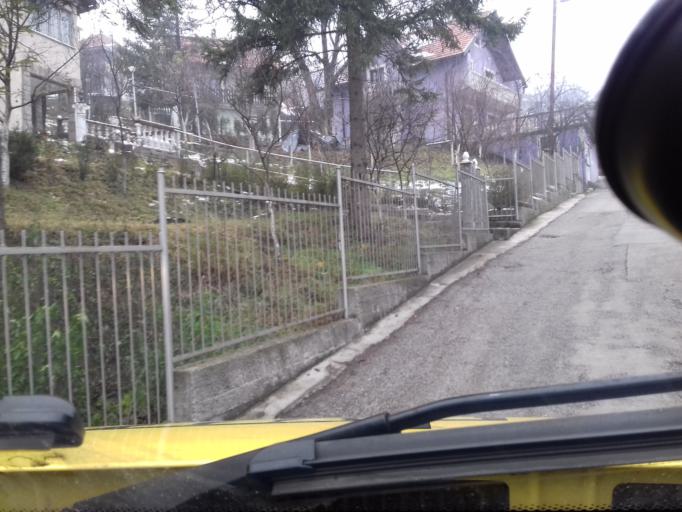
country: BA
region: Federation of Bosnia and Herzegovina
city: Zenica
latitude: 44.1990
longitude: 17.8956
